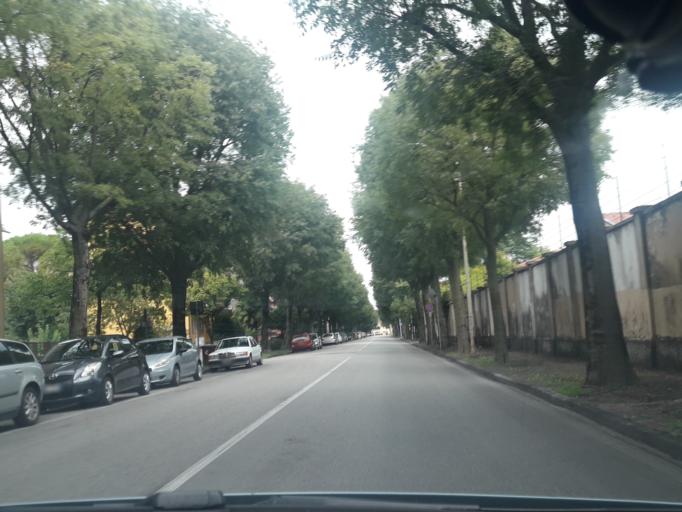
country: IT
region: Friuli Venezia Giulia
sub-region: Provincia di Udine
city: Udine
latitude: 46.0674
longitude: 13.2545
